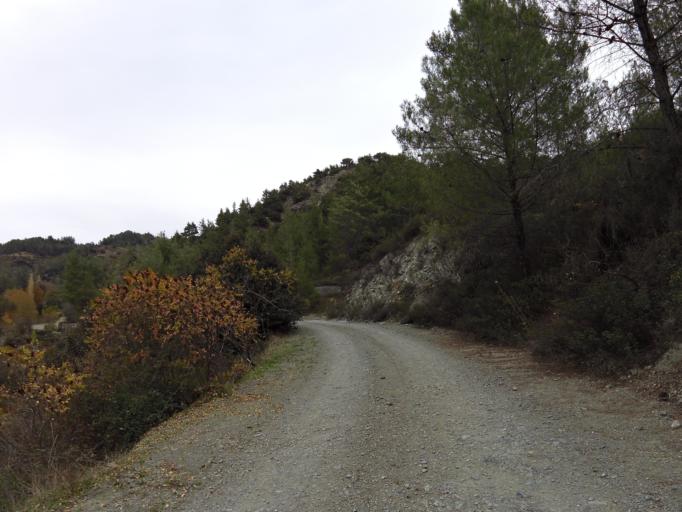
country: CY
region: Limassol
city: Kyperounta
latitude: 34.9240
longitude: 32.9453
